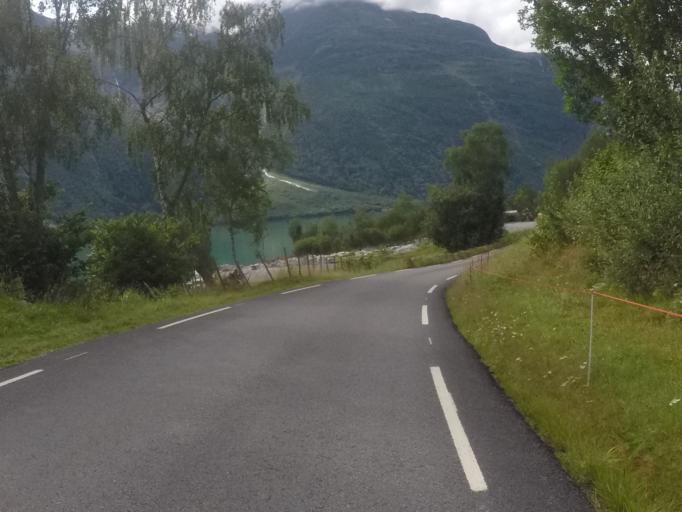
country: NO
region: Sogn og Fjordane
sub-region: Stryn
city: Stryn
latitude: 61.8252
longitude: 6.9732
